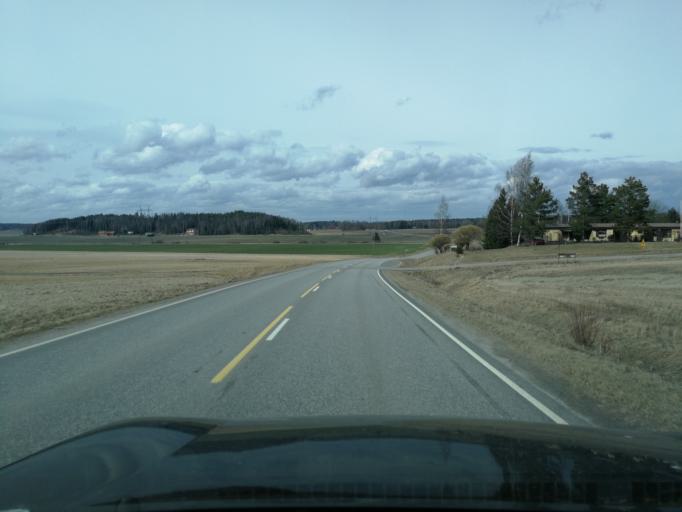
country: FI
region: Uusimaa
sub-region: Helsinki
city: Siuntio
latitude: 60.1113
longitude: 24.2416
